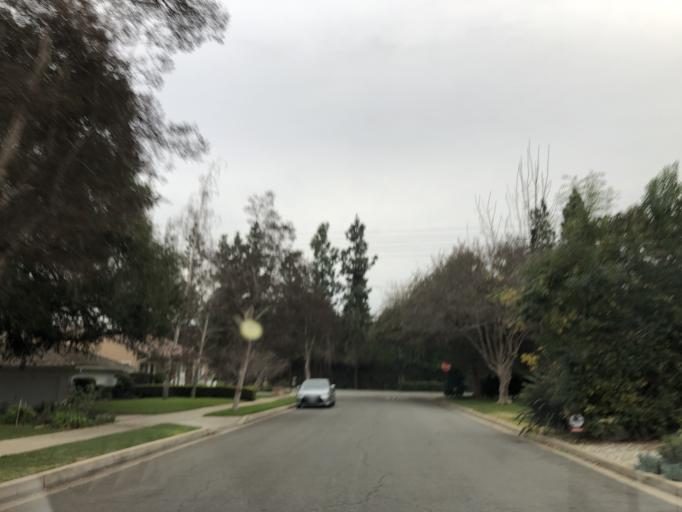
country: US
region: California
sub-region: Los Angeles County
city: San Marino
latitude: 34.1141
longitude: -118.0983
